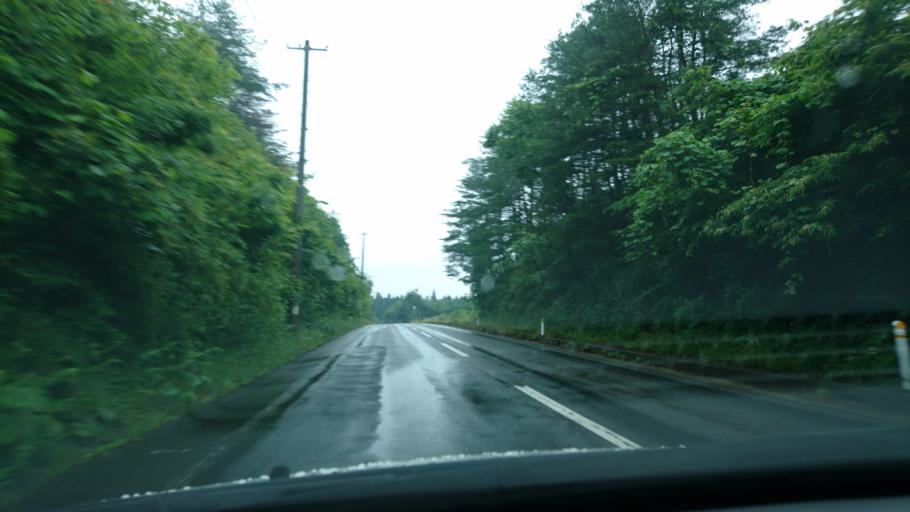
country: JP
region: Iwate
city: Ichinoseki
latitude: 38.9352
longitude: 141.0531
